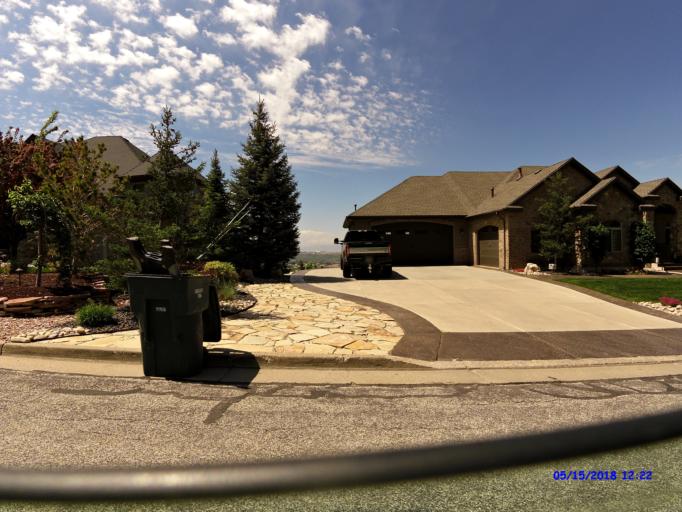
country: US
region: Utah
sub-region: Weber County
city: Uintah
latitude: 41.1659
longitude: -111.9220
